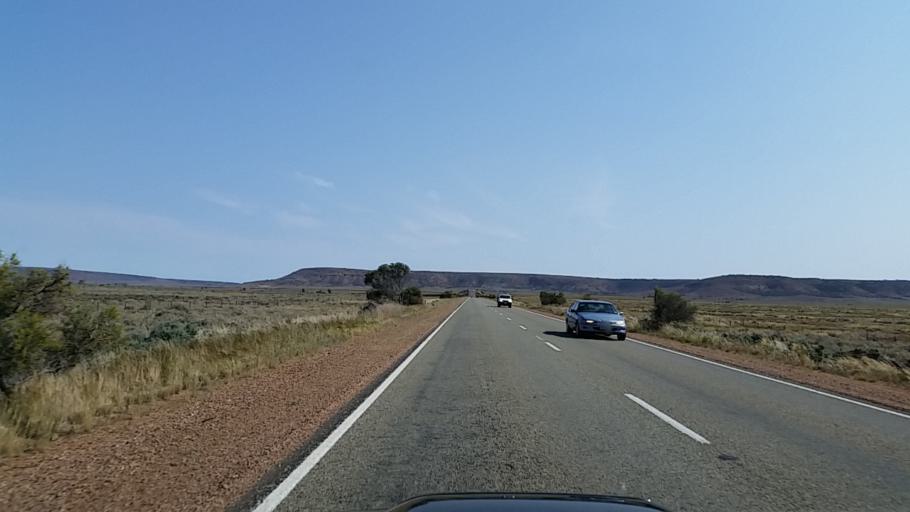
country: AU
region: South Australia
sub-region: Port Augusta
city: Port Augusta West
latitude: -32.5340
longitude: 137.6537
